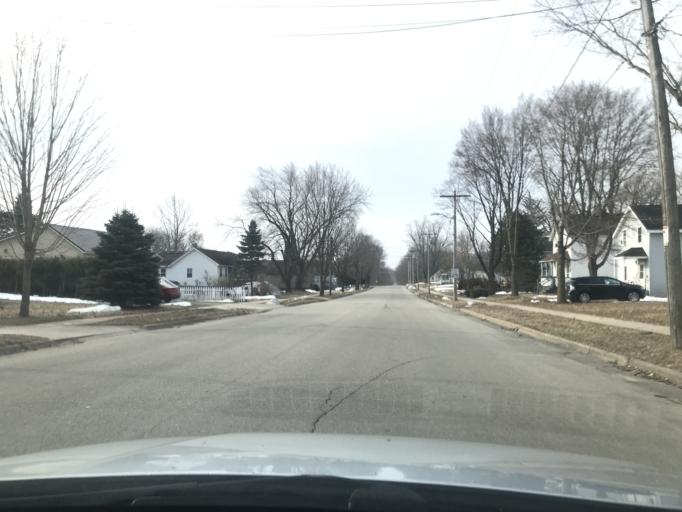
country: US
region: Wisconsin
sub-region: Oconto County
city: Oconto Falls
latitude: 44.8704
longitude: -88.1467
